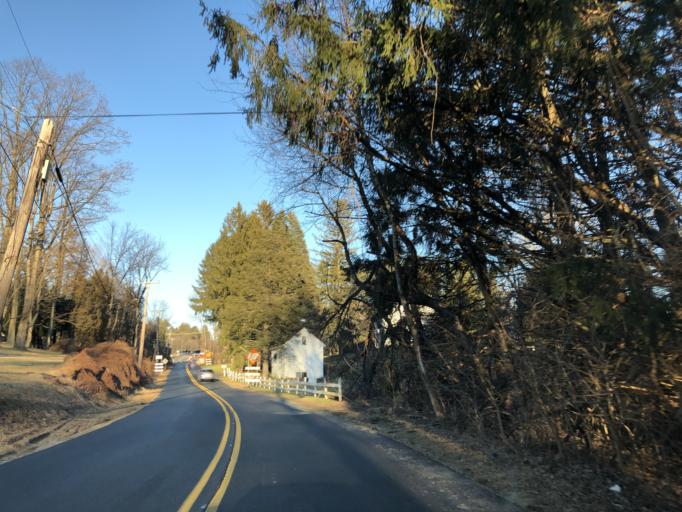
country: US
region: Pennsylvania
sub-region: Delaware County
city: Chester Heights
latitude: 39.8641
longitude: -75.4953
